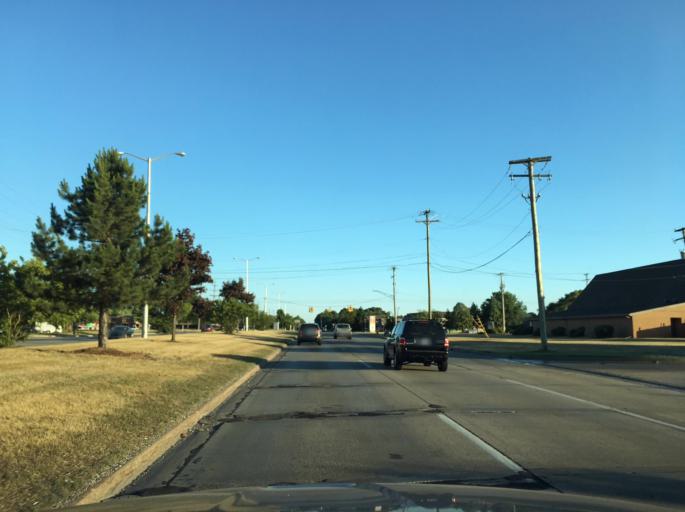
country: US
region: Michigan
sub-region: Macomb County
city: Utica
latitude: 42.6117
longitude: -82.9924
